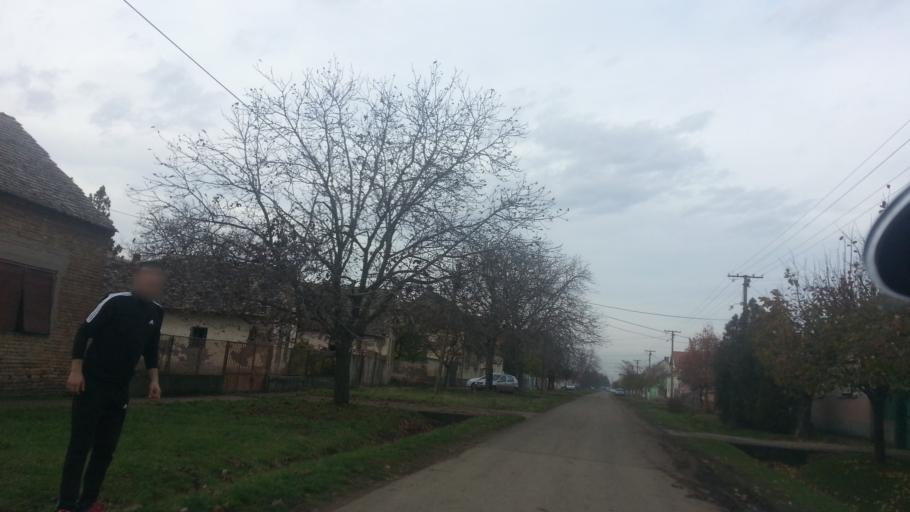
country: RS
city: Putinci
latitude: 44.9611
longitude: 19.9749
